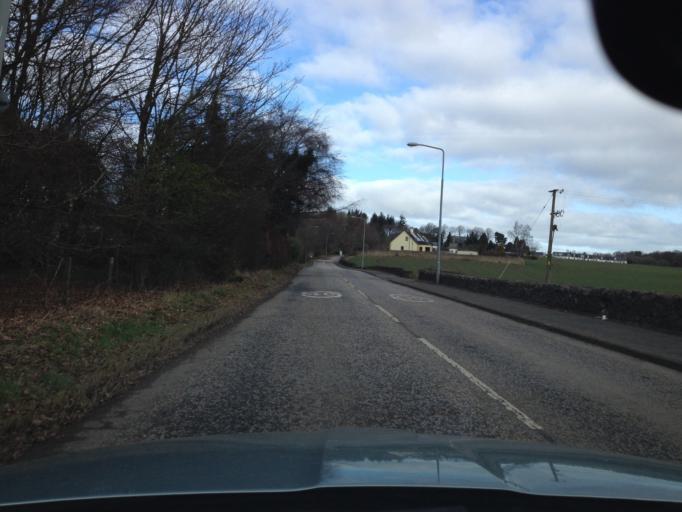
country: GB
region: Scotland
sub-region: West Lothian
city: Mid Calder
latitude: 55.8997
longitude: -3.4859
